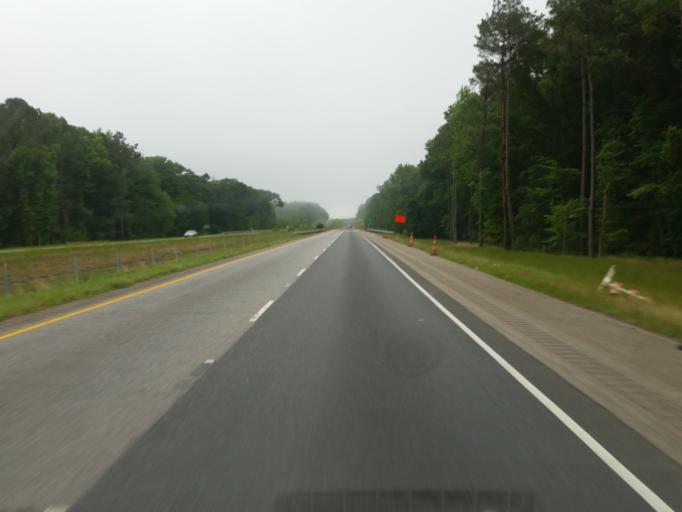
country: US
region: Louisiana
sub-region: Webster Parish
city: Minden
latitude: 32.5658
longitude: -93.1775
